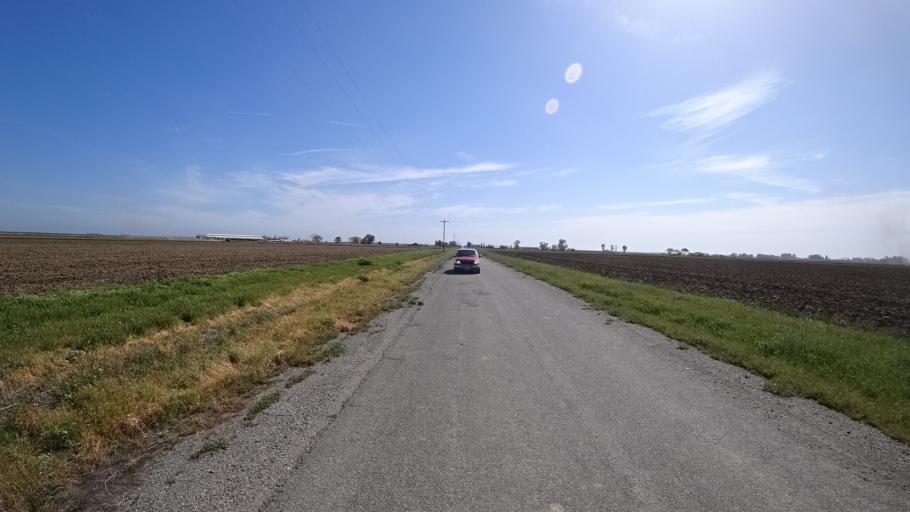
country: US
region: California
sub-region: Glenn County
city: Hamilton City
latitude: 39.6162
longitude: -122.0730
